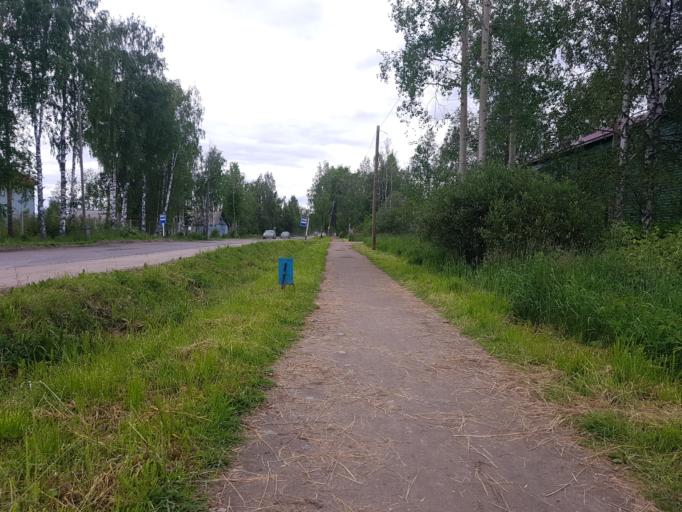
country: RU
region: Republic of Karelia
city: Kalevala
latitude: 65.2020
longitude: 31.1758
